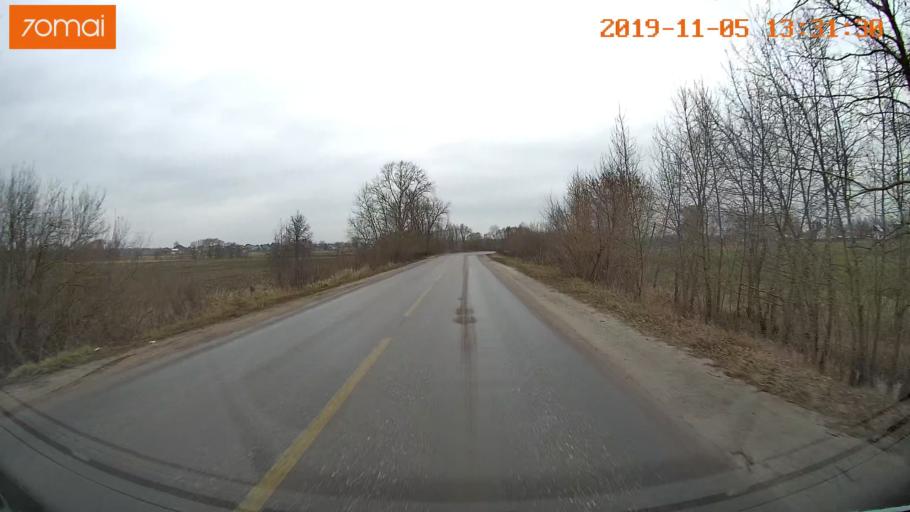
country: RU
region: Ivanovo
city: Shuya
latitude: 56.8765
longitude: 41.3935
